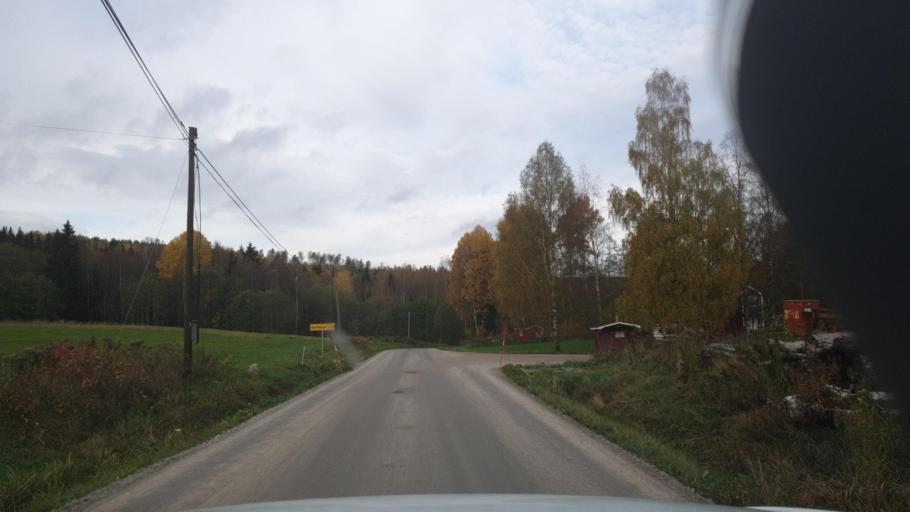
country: SE
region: Vaermland
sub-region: Sunne Kommun
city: Sunne
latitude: 59.6905
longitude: 12.8890
